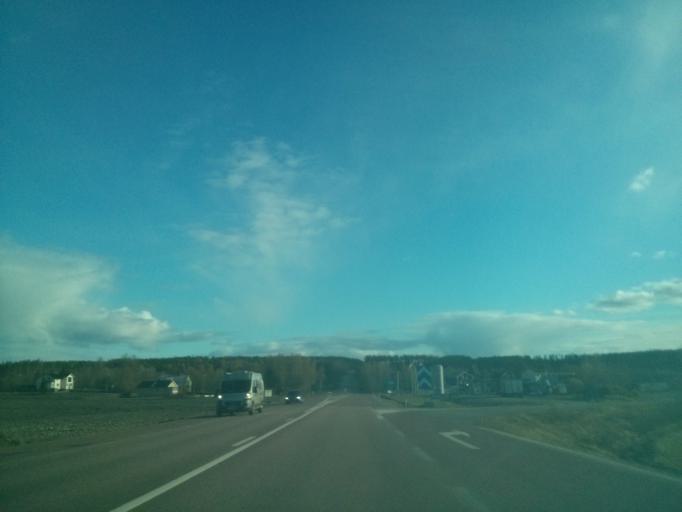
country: SE
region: Gaevleborg
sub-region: Nordanstigs Kommun
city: Bergsjoe
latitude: 62.0468
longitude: 17.2668
